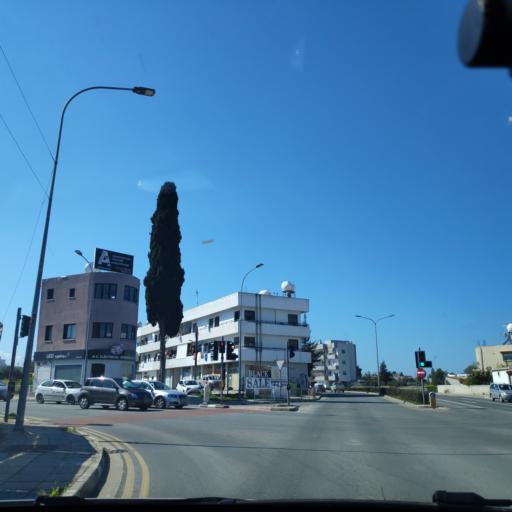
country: CY
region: Lefkosia
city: Kato Deftera
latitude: 35.1111
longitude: 33.3062
